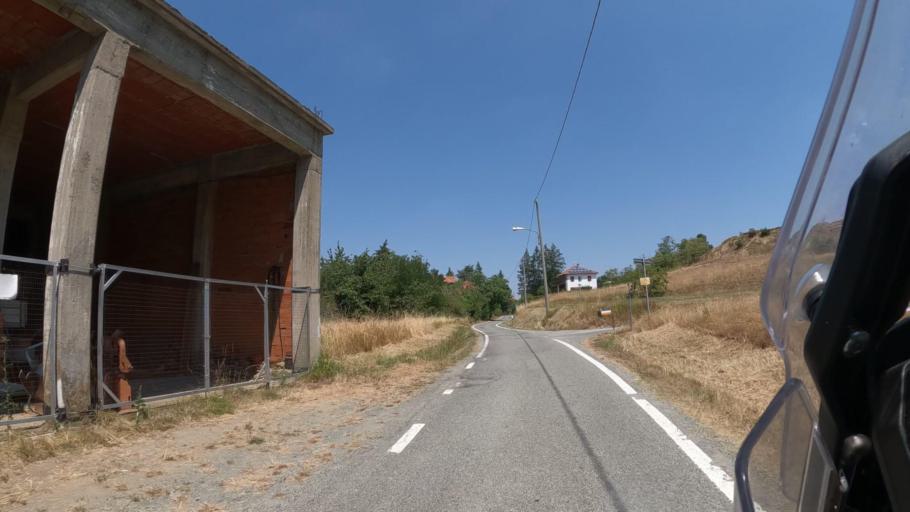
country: IT
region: Piedmont
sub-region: Provincia di Alessandria
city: Ponzone
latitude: 44.5481
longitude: 8.4821
